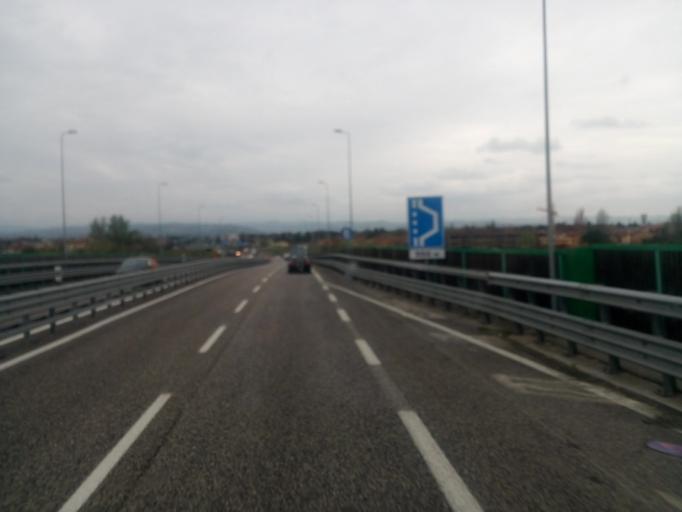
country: IT
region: Emilia-Romagna
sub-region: Forli-Cesena
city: Forli
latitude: 44.2156
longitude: 12.0745
